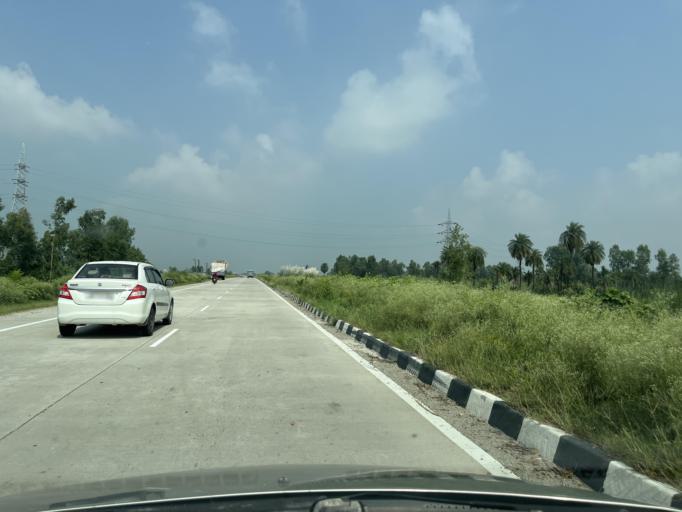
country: IN
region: Uttarakhand
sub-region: Udham Singh Nagar
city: Kashipur
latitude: 29.1657
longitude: 78.9588
